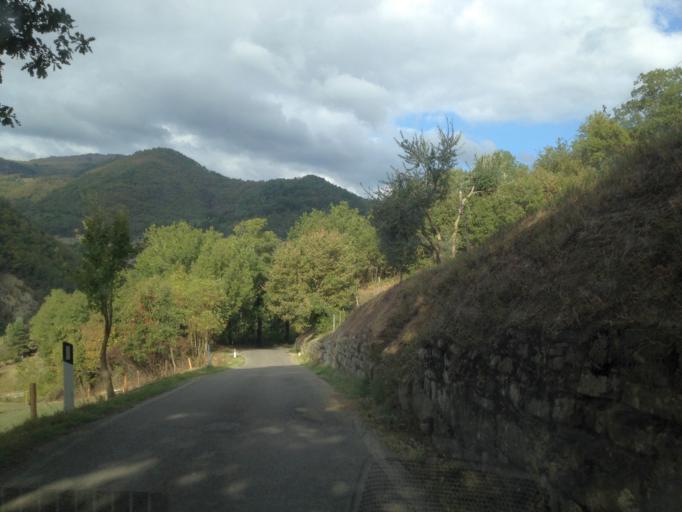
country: IT
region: Tuscany
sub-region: Province of Florence
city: Montebonello
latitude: 43.8545
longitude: 11.4983
